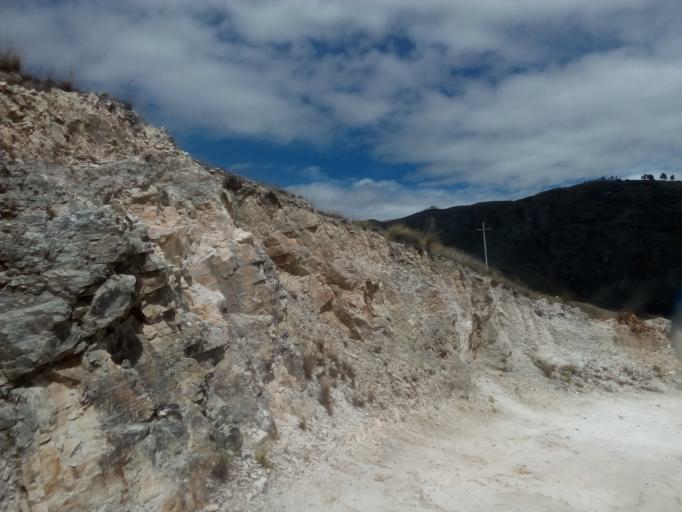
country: PE
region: La Libertad
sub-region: Sanchez Carrion
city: Curgos
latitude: -7.7995
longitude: -77.9766
